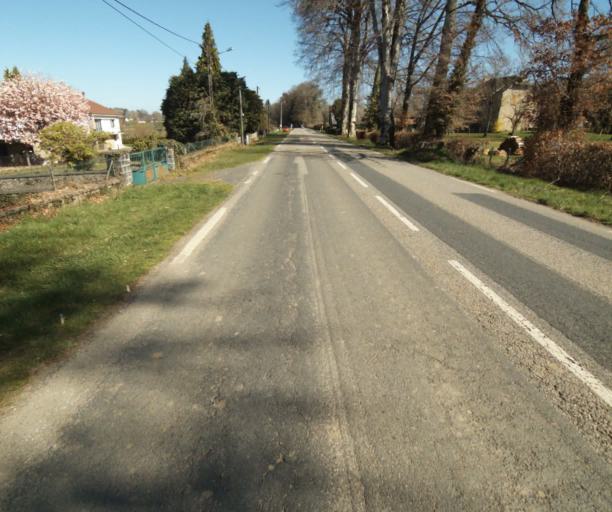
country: FR
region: Limousin
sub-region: Departement de la Correze
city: Seilhac
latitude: 45.3662
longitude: 1.7254
